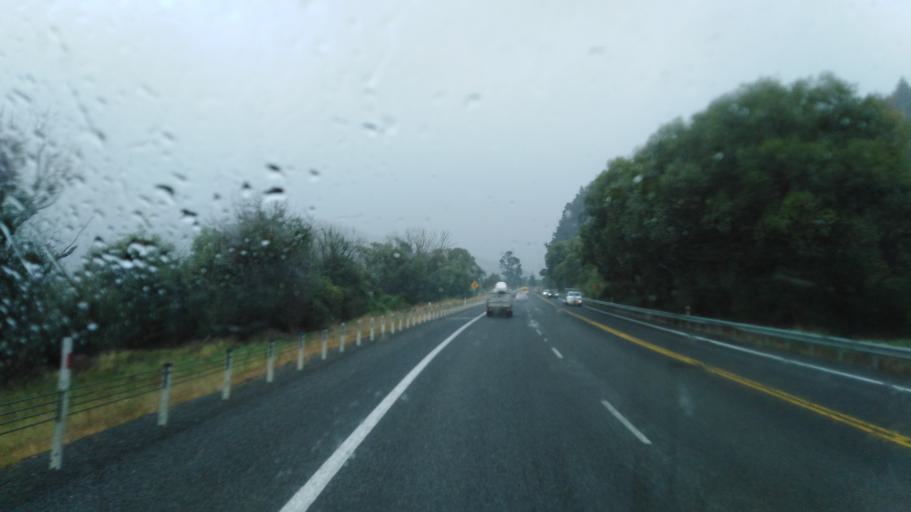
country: NZ
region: Marlborough
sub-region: Marlborough District
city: Picton
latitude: -41.3785
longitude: 173.9468
